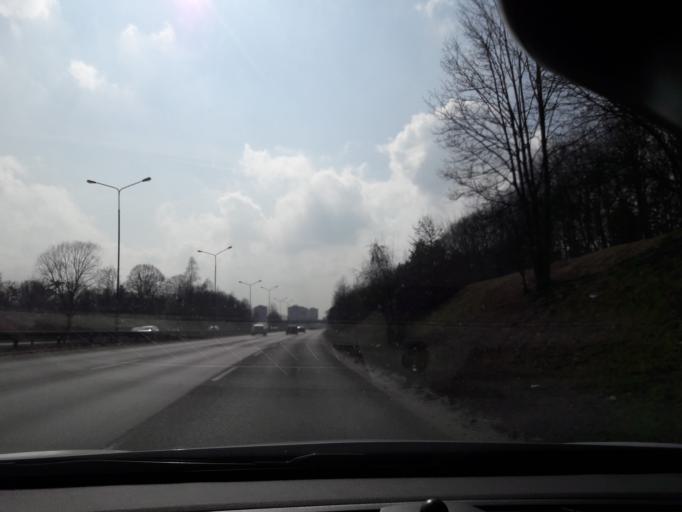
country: PL
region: Greater Poland Voivodeship
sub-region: Poznan
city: Poznan
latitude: 52.4390
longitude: 16.9091
